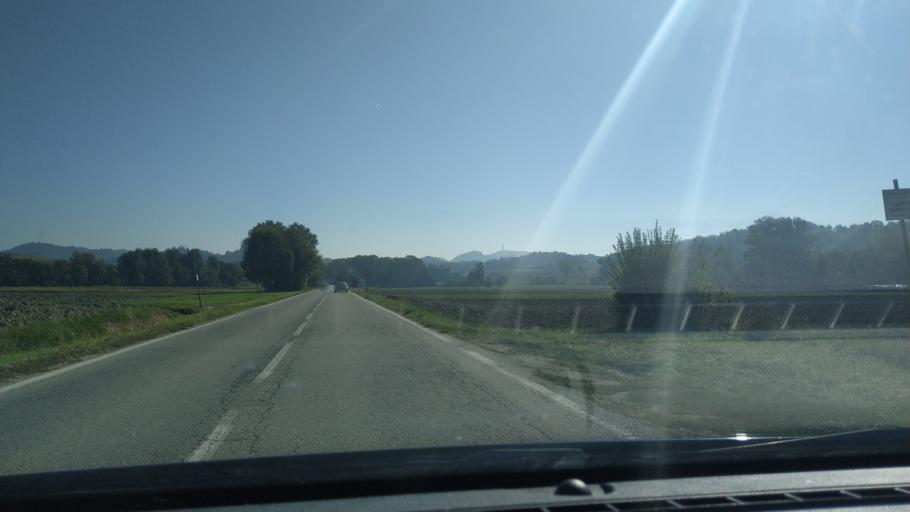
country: IT
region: Piedmont
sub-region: Provincia di Asti
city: Robella
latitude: 45.0861
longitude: 8.1132
